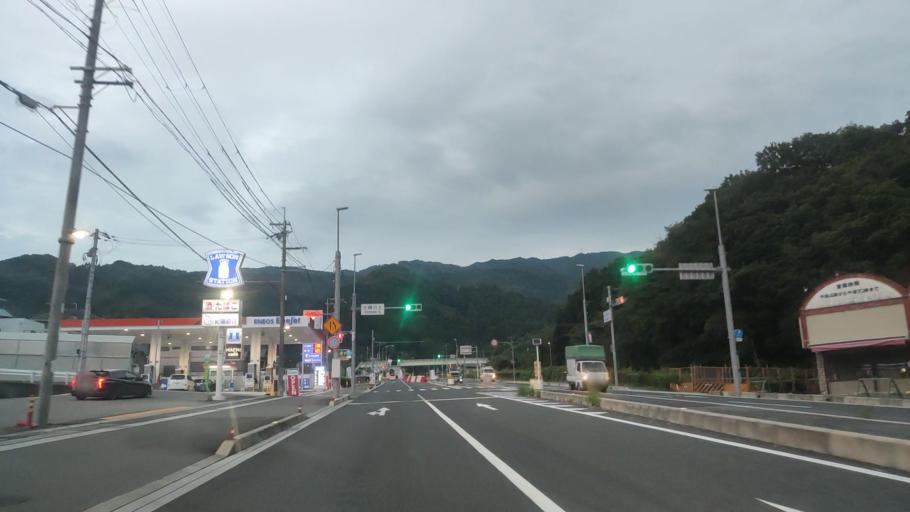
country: JP
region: Wakayama
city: Hashimoto
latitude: 34.3665
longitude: 135.6068
